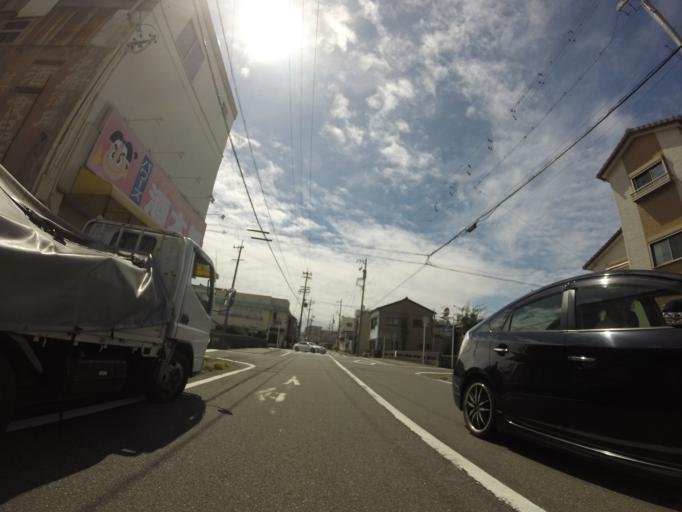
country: JP
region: Shizuoka
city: Yaizu
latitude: 34.8700
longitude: 138.3238
